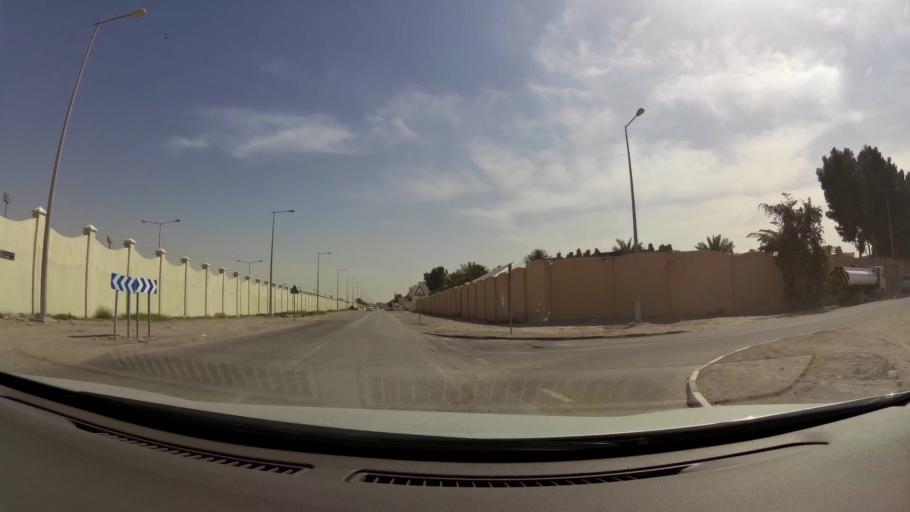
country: QA
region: Baladiyat ar Rayyan
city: Ar Rayyan
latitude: 25.2766
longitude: 51.4261
